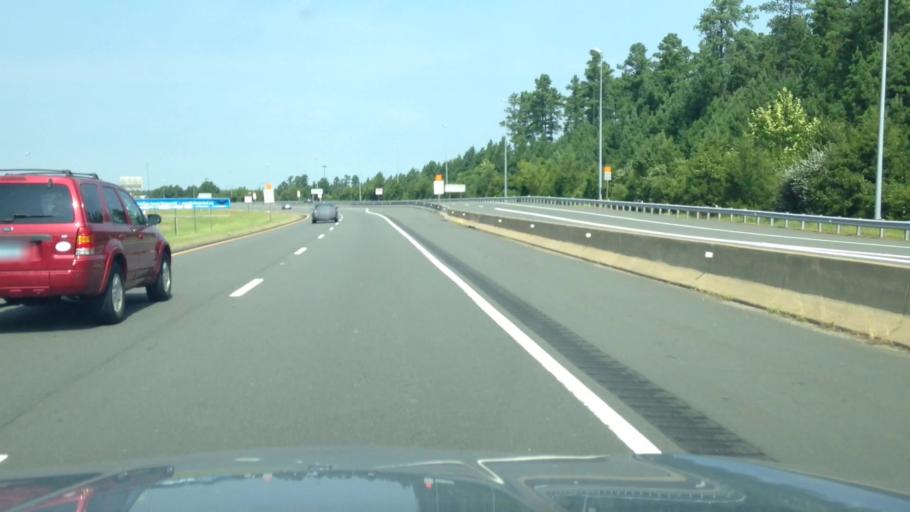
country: US
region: Virginia
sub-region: Loudoun County
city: Oak Grove
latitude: 38.9718
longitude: -77.4367
